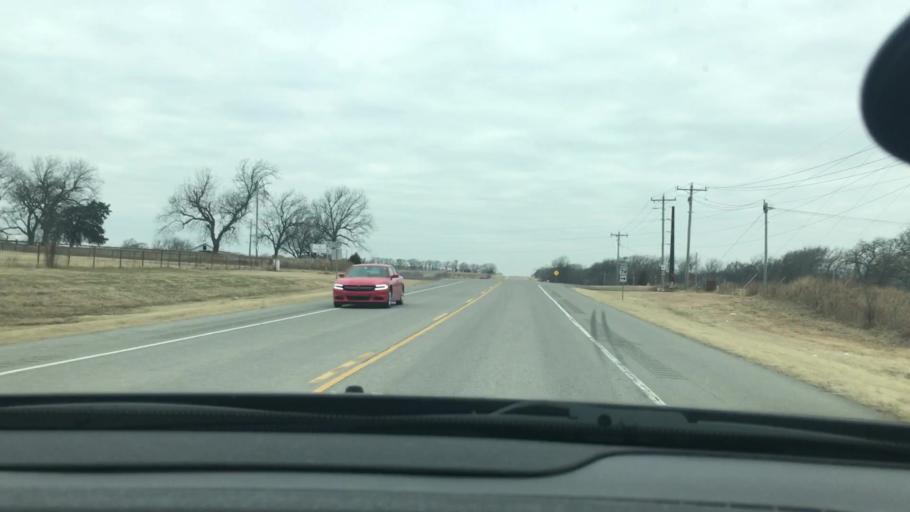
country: US
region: Oklahoma
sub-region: Carter County
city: Healdton
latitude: 34.4925
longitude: -97.4038
